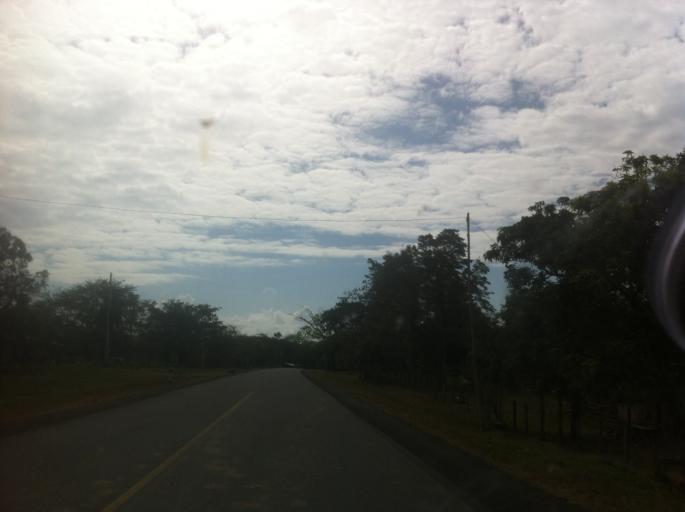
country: NI
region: Rio San Juan
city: San Miguelito
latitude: 11.3187
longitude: -84.7345
